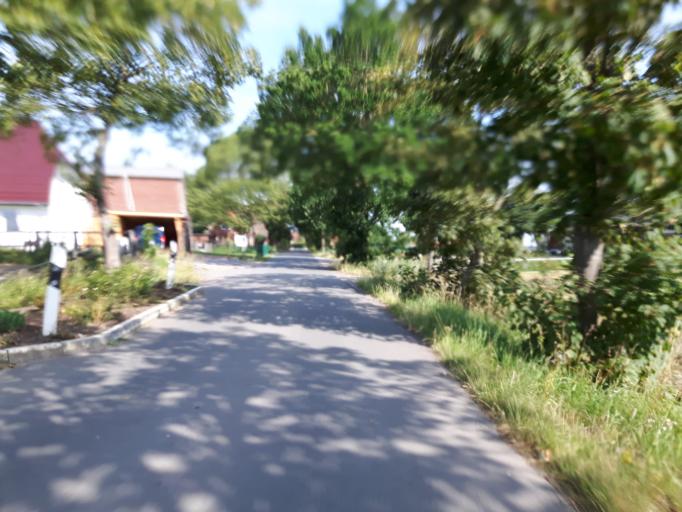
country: DE
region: Lower Saxony
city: Elsfleth
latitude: 53.1975
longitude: 8.4812
